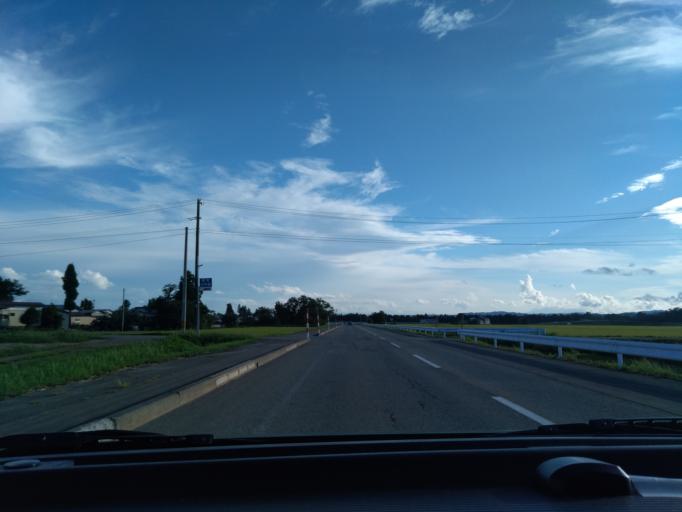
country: JP
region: Akita
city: Omagari
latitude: 39.4059
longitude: 140.4762
